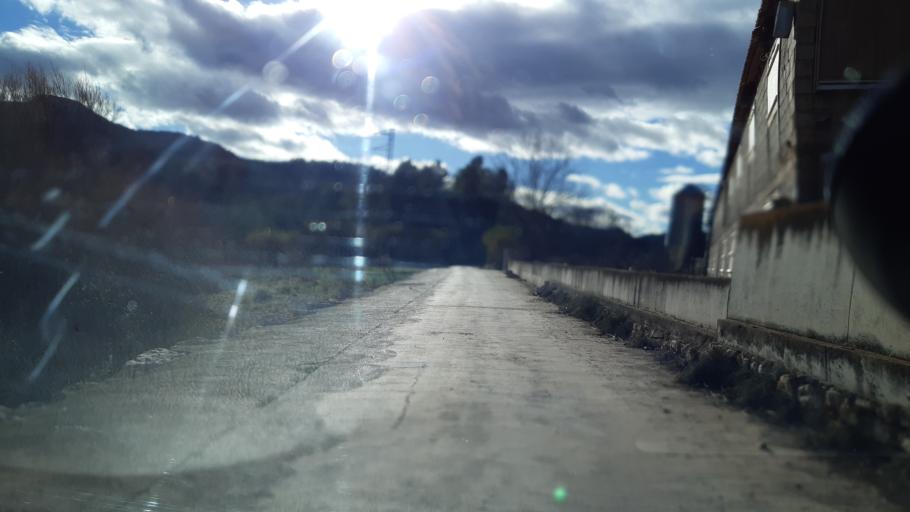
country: ES
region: Aragon
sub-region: Provincia de Teruel
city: Valderrobres
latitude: 40.8444
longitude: 0.2048
